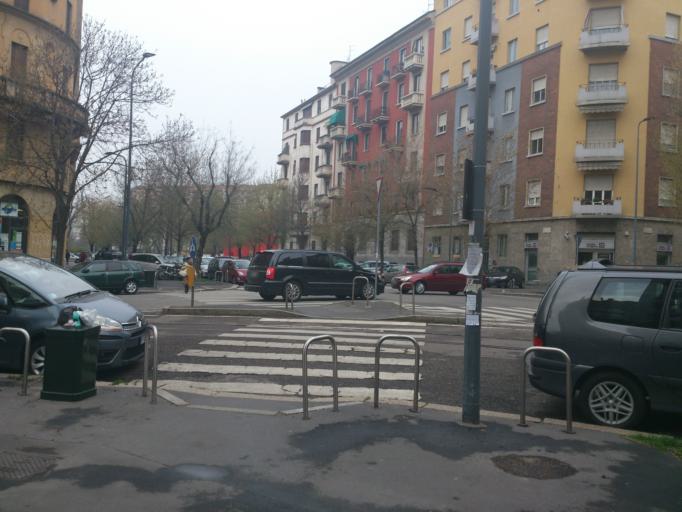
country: IT
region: Lombardy
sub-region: Citta metropolitana di Milano
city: Romano Banco
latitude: 45.4650
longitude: 9.1400
